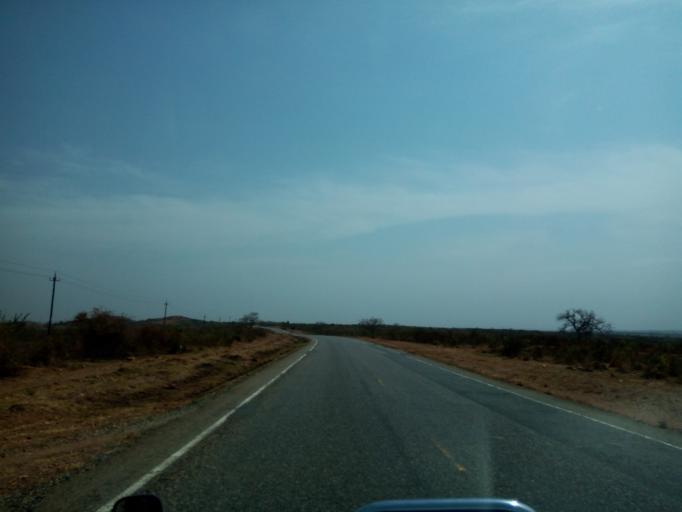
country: UG
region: Northern Region
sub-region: Nebbi District
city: Nebbi
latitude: 2.4469
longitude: 31.2566
